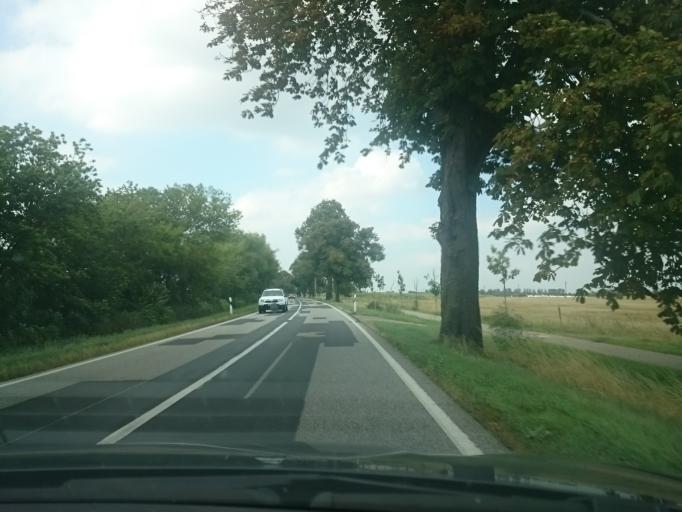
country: DE
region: Mecklenburg-Vorpommern
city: Ducherow
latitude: 53.7469
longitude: 13.7823
